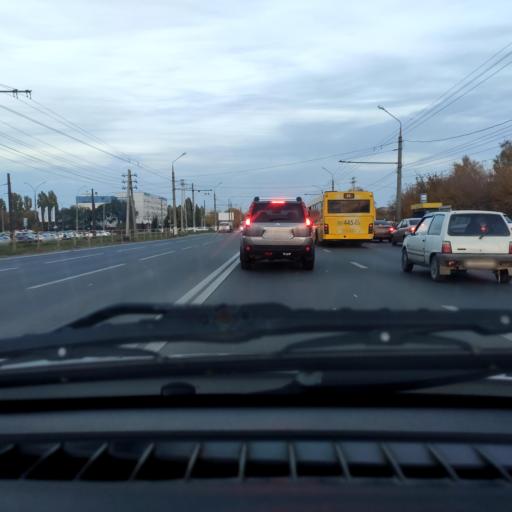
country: RU
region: Samara
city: Tol'yatti
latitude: 53.5523
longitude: 49.3000
